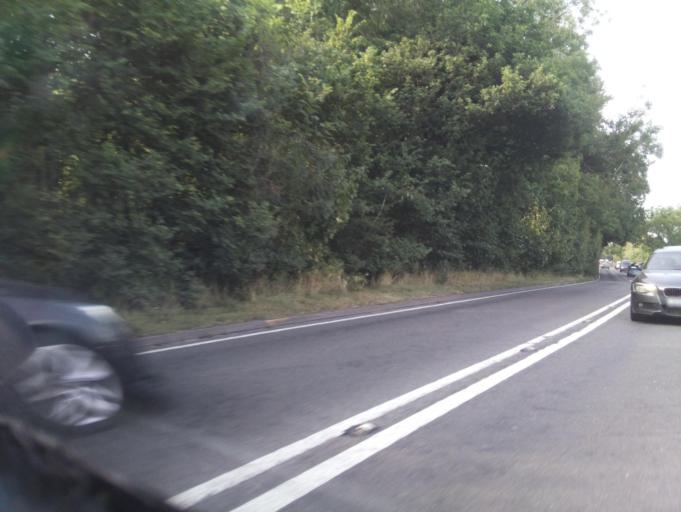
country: GB
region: England
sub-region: Warwickshire
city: Studley
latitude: 52.3021
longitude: -1.8753
